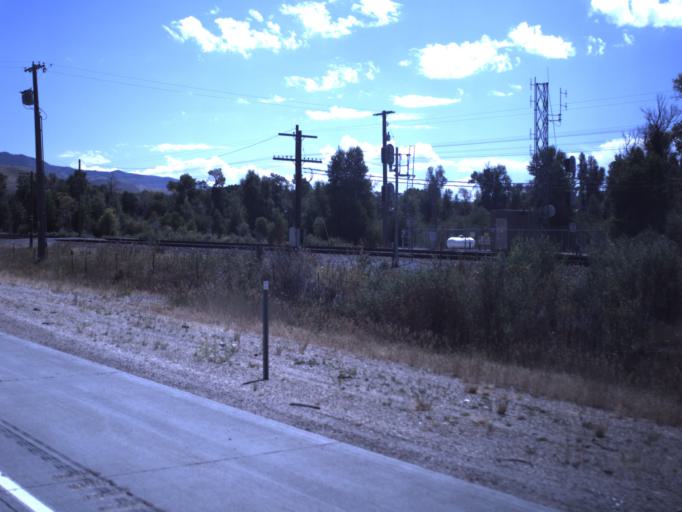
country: US
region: Utah
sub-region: Morgan County
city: Mountain Green
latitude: 41.1372
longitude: -111.7950
